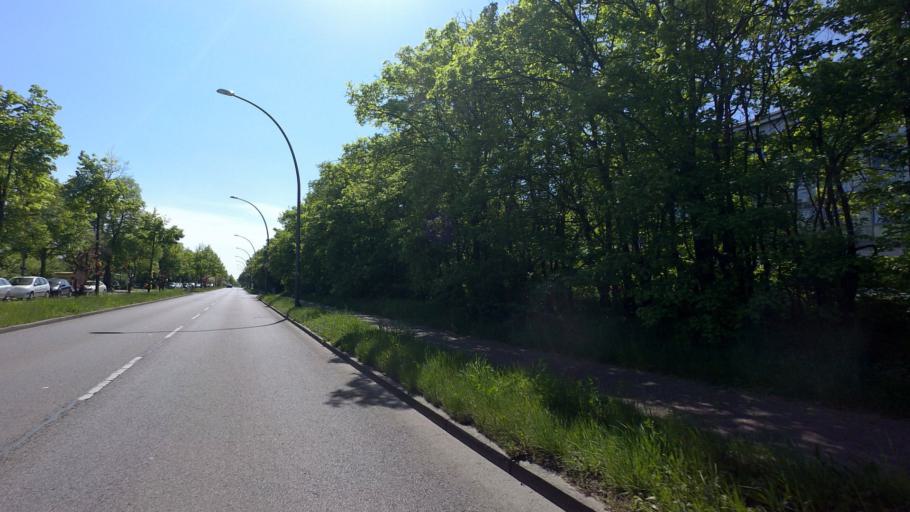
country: DE
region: Brandenburg
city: Schonefeld
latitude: 52.4033
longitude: 13.5117
